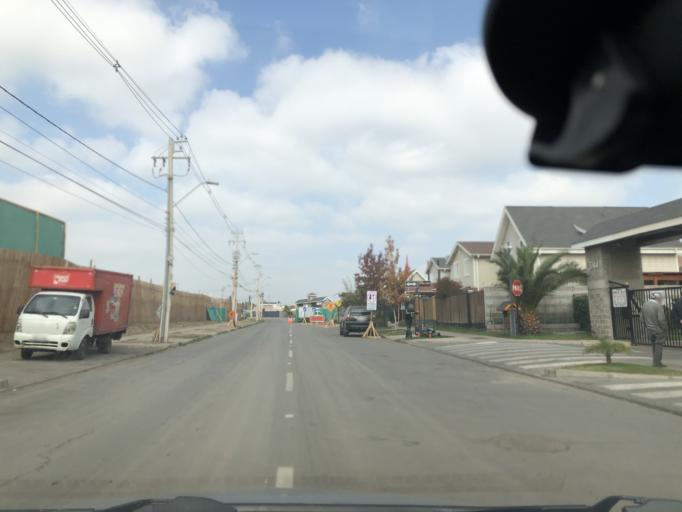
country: CL
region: Santiago Metropolitan
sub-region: Provincia de Cordillera
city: Puente Alto
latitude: -33.5754
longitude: -70.5938
